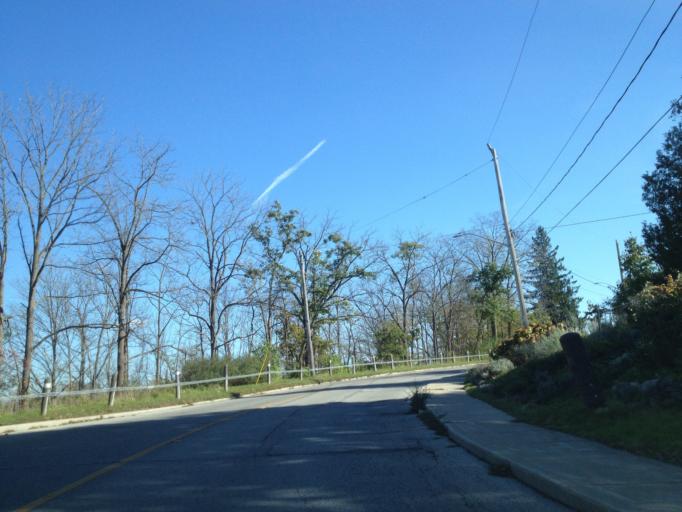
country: CA
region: Ontario
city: St. Thomas
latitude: 42.7792
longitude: -81.2108
